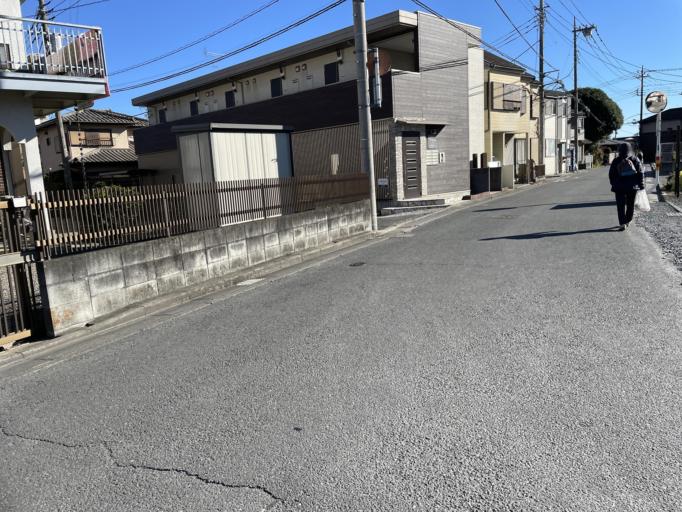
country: JP
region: Saitama
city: Sakado
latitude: 35.9392
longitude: 139.4274
